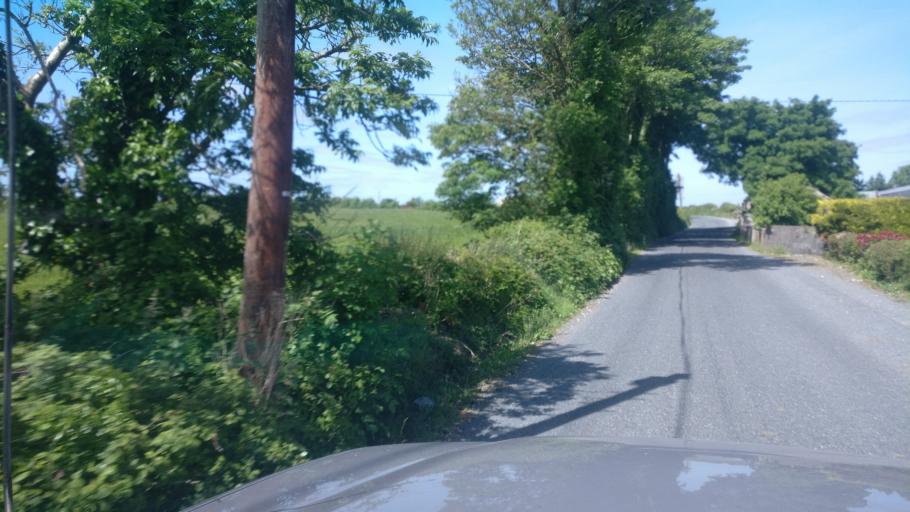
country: IE
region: Connaught
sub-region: County Galway
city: Gort
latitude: 53.0754
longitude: -8.7973
